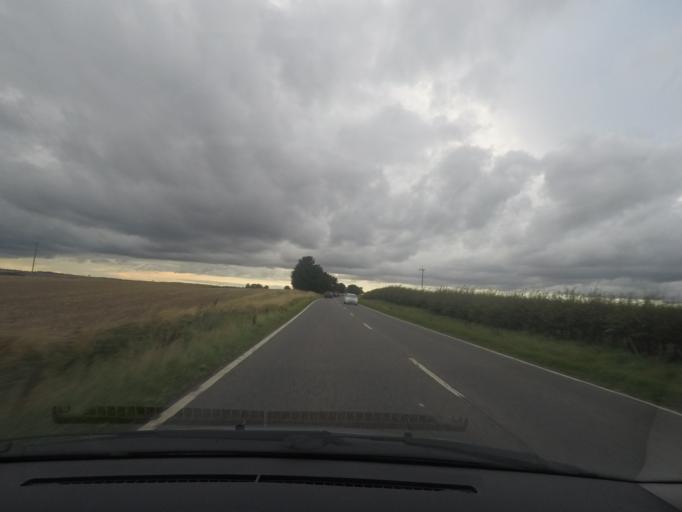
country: GB
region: England
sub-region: Lincolnshire
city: Burwell
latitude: 53.3078
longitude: 0.0192
